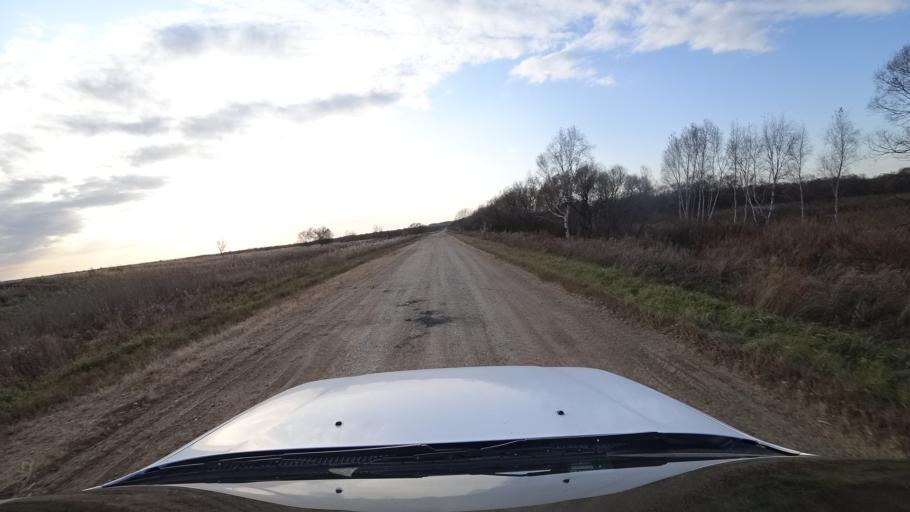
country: RU
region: Primorskiy
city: Lazo
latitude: 45.8253
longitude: 133.6080
